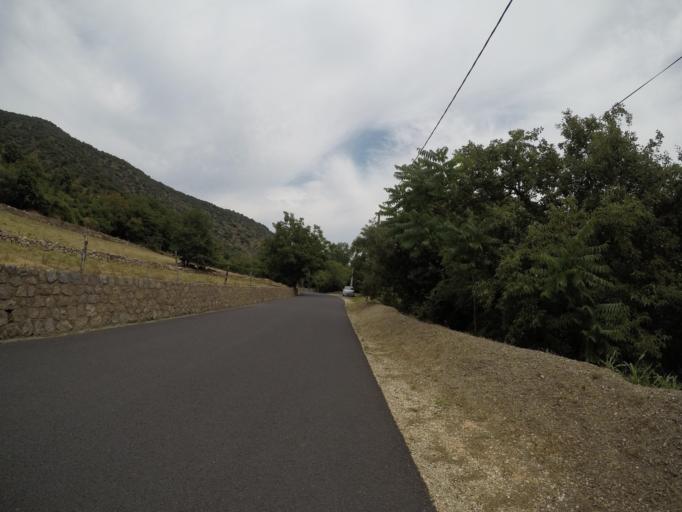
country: FR
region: Languedoc-Roussillon
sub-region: Departement des Pyrenees-Orientales
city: Ria-Sirach
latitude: 42.6027
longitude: 2.3835
